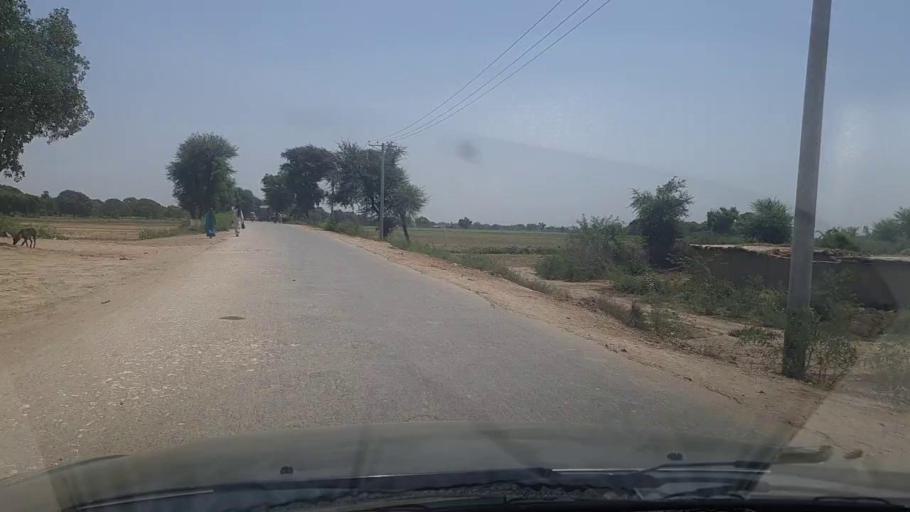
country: PK
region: Sindh
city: Chambar
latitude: 25.2639
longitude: 68.6494
